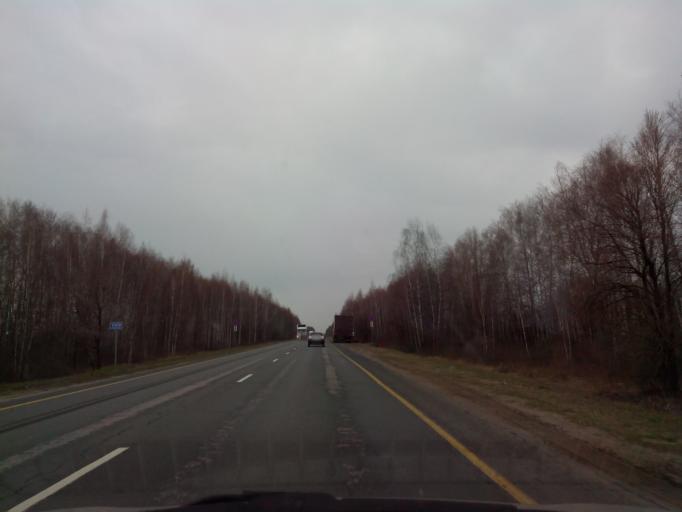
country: RU
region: Tambov
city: Michurinsk
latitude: 53.0626
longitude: 40.4466
